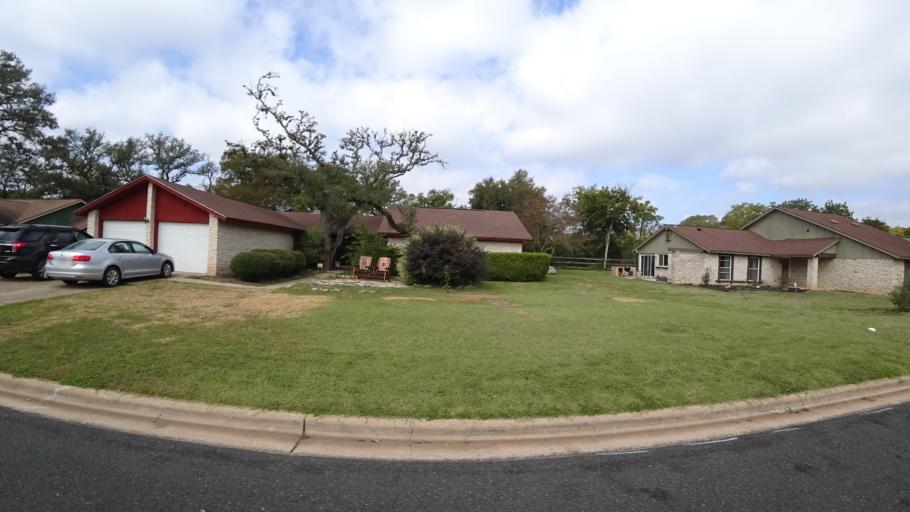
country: US
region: Texas
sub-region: Travis County
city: Shady Hollow
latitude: 30.2154
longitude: -97.8370
